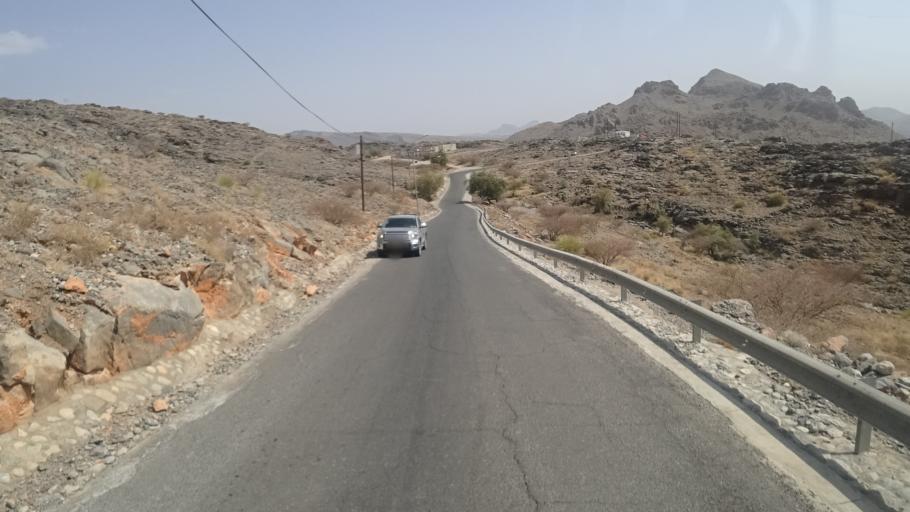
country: OM
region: Muhafazat ad Dakhiliyah
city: Bahla'
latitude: 23.1306
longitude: 57.3043
